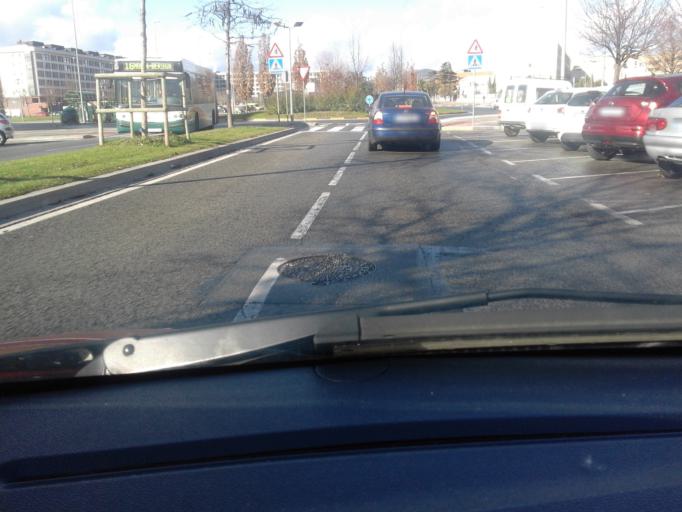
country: ES
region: Navarre
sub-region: Provincia de Navarra
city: Berriozar
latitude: 42.8272
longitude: -1.6607
